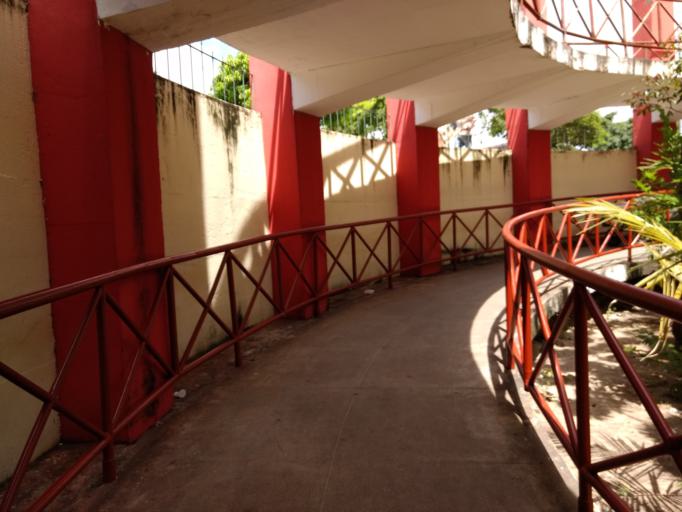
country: BR
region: Ceara
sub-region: Fortaleza
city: Fortaleza
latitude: -3.7304
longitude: -38.5389
